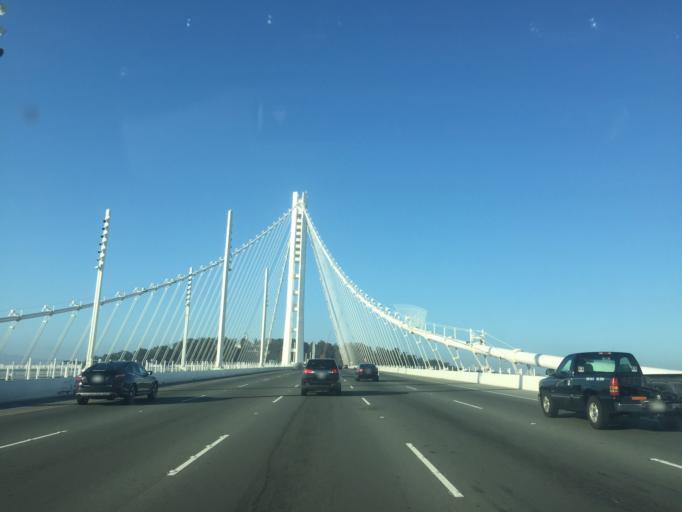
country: US
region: California
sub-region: Alameda County
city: Emeryville
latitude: 37.8173
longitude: -122.3553
